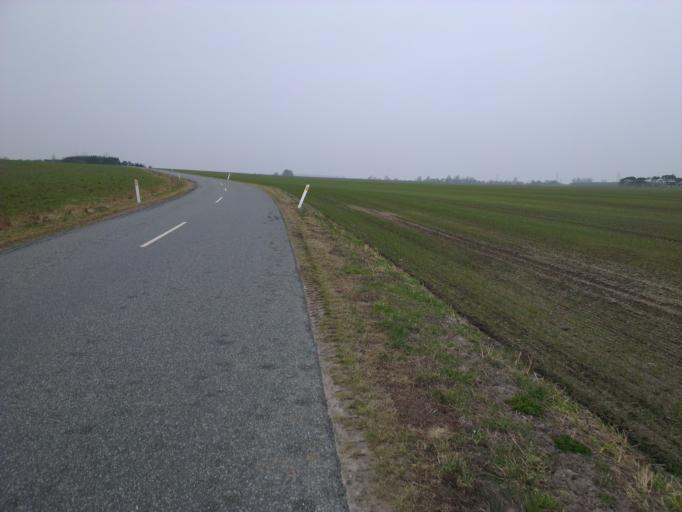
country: DK
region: Capital Region
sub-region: Frederikssund Kommune
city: Skibby
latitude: 55.7887
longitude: 11.9955
